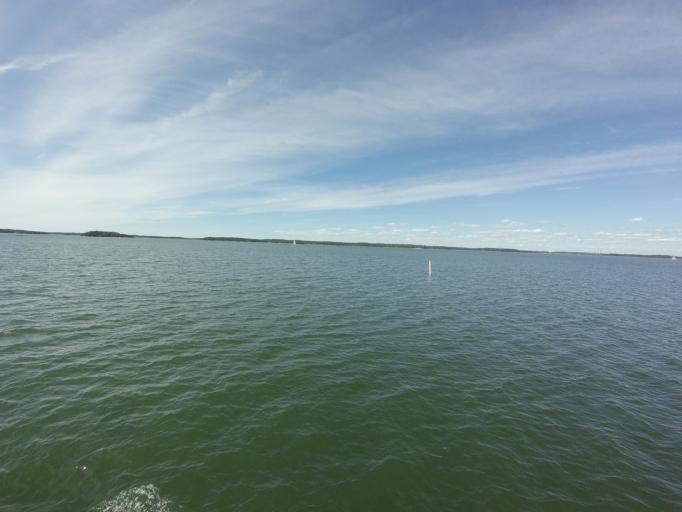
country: FI
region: Varsinais-Suomi
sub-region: Turku
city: Naantali
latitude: 60.3833
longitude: 22.0852
